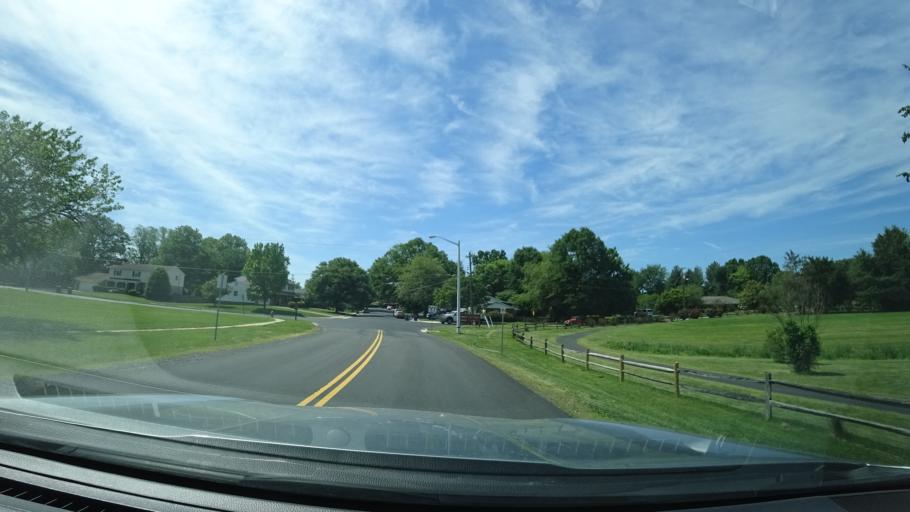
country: US
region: Virginia
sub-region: Fairfax County
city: Herndon
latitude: 38.9710
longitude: -77.3946
